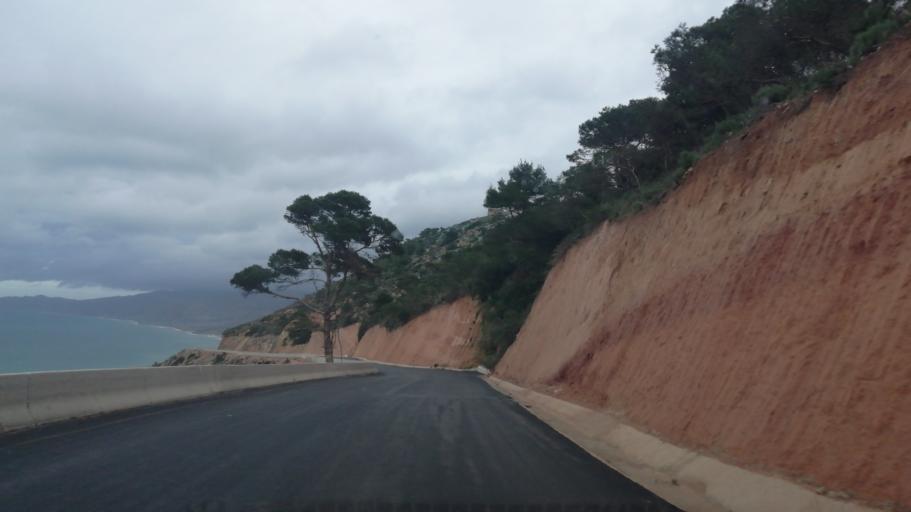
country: DZ
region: Oran
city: Bir el Djir
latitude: 35.7618
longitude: -0.5286
